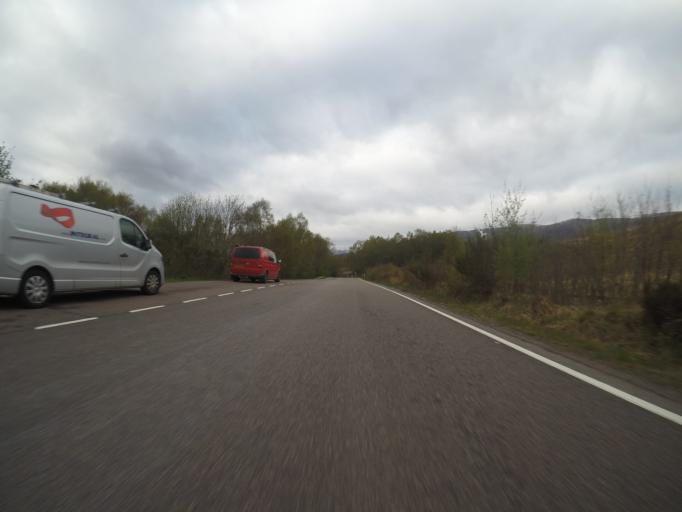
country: GB
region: Scotland
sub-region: Highland
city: Kingussie
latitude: 56.9722
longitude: -4.4263
